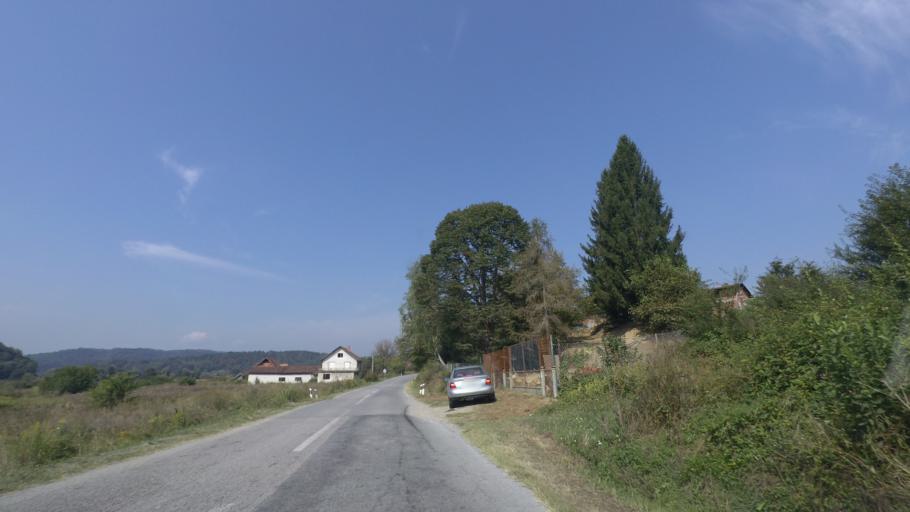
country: HR
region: Sisacko-Moslavacka
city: Dvor
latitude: 45.0809
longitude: 16.3420
